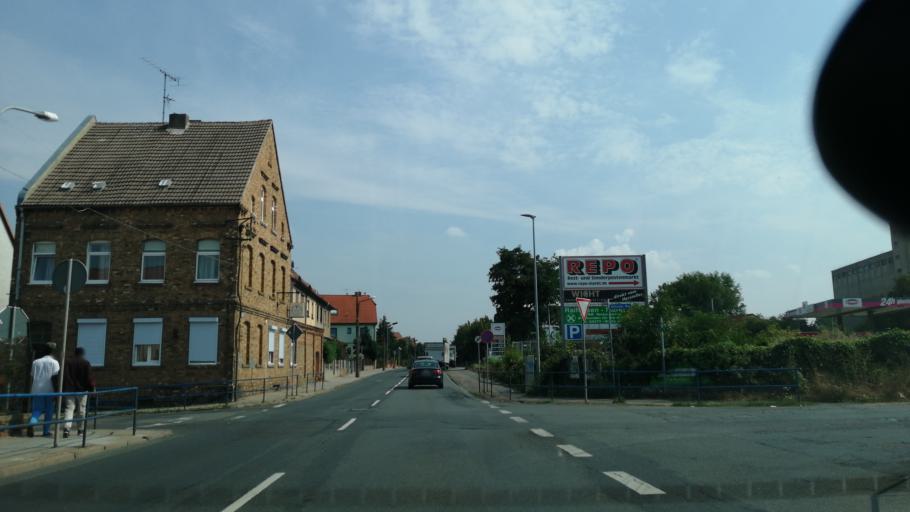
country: DE
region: Saxony-Anhalt
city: Wimmelburg
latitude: 51.5222
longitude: 11.5411
